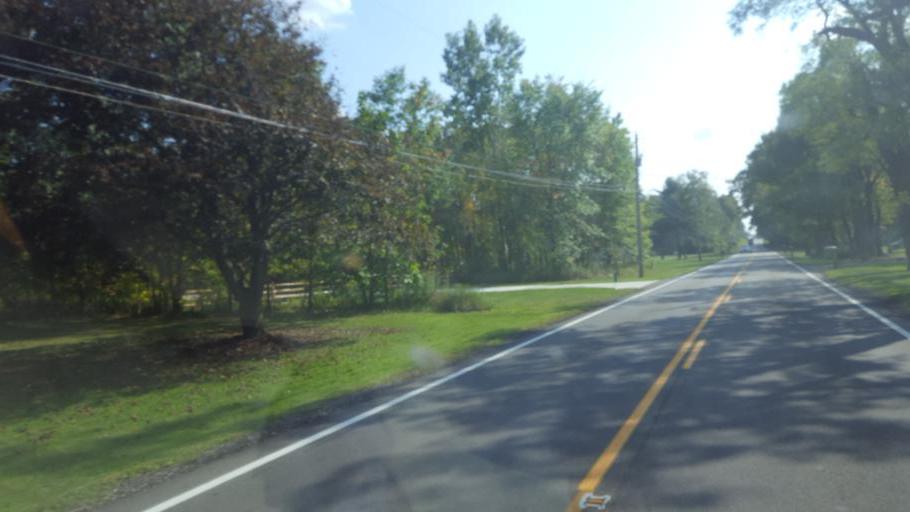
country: US
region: Ohio
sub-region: Richland County
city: Ontario
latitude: 40.7725
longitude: -82.6548
